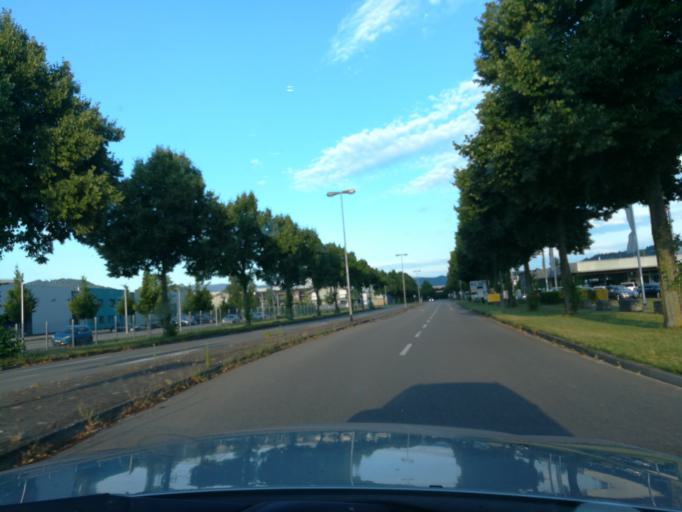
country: DE
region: Baden-Wuerttemberg
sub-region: Freiburg Region
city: Offenburg
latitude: 48.4398
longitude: 7.9284
